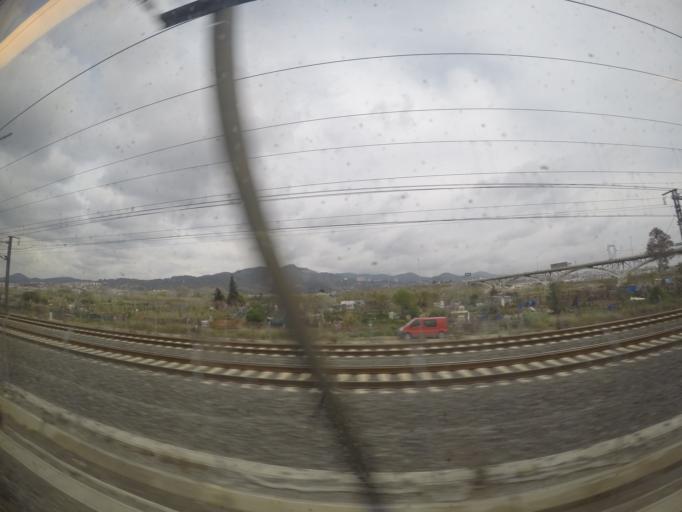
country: ES
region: Catalonia
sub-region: Provincia de Barcelona
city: Sant Vicenc dels Horts
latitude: 41.3913
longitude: 2.0193
